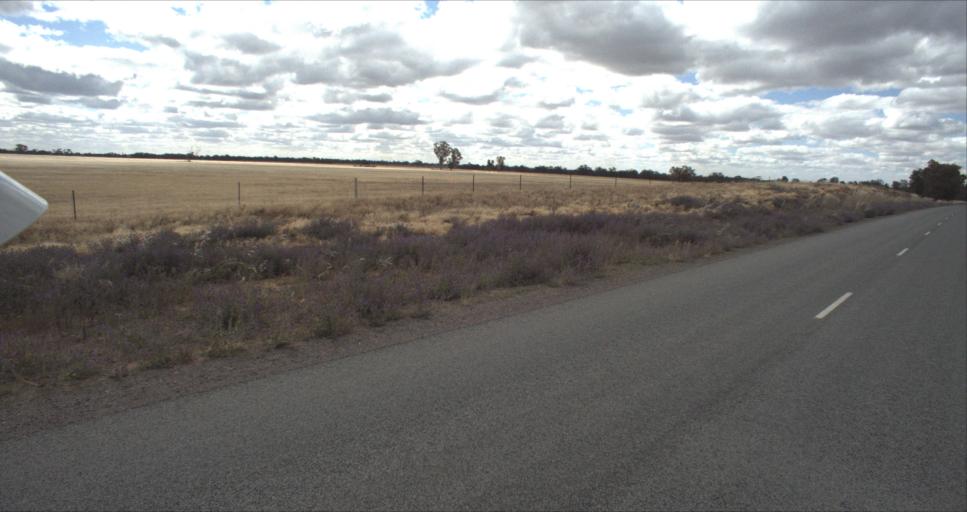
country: AU
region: New South Wales
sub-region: Leeton
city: Leeton
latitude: -34.6747
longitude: 146.3468
